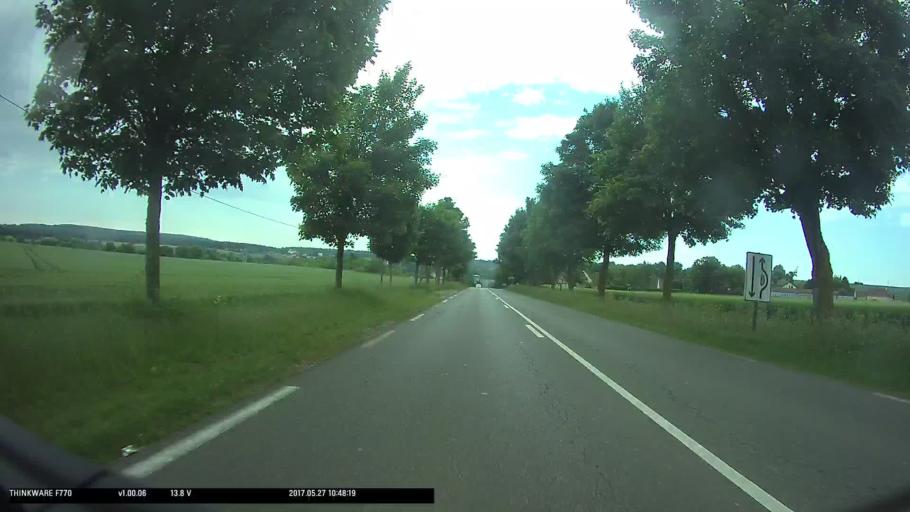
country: FR
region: Ile-de-France
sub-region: Departement du Val-d'Oise
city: Chars
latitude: 49.1635
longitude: 1.9287
